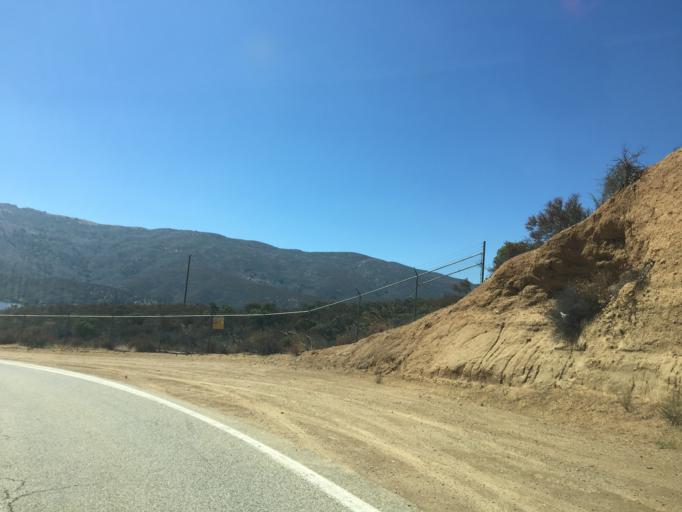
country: US
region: California
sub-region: Los Angeles County
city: Green Valley
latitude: 34.5911
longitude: -118.3842
